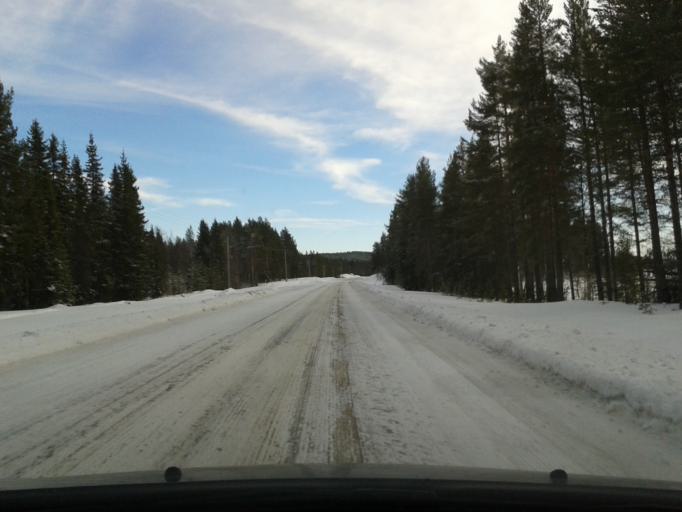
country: SE
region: Vaesterbotten
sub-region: Vilhelmina Kommun
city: Vilhelmina
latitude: 64.3866
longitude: 16.8845
